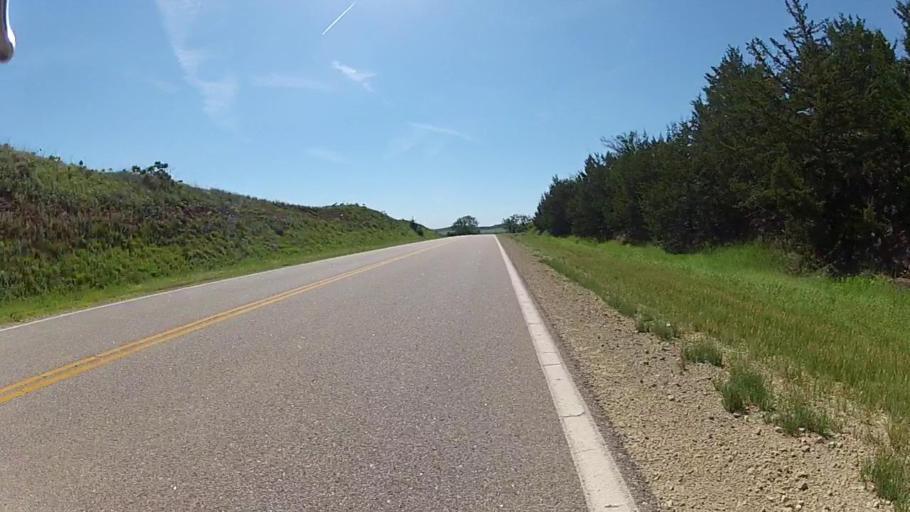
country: US
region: Kansas
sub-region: Barber County
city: Medicine Lodge
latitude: 37.2783
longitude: -98.7397
